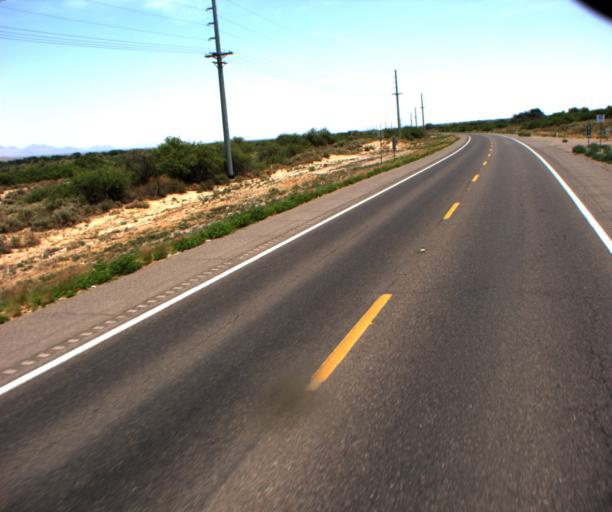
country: US
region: Arizona
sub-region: Graham County
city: Pima
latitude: 32.9411
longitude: -109.9072
